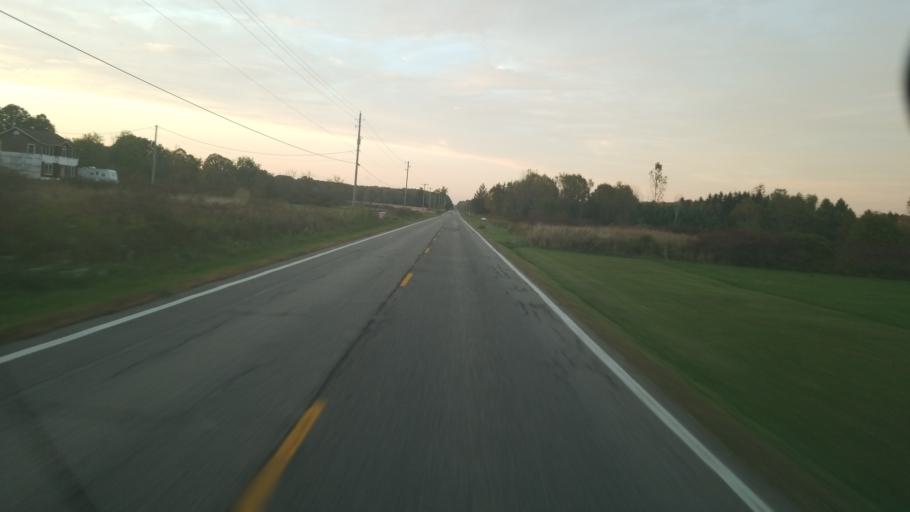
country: US
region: Ohio
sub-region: Ashtabula County
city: Andover
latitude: 41.6381
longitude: -80.6669
